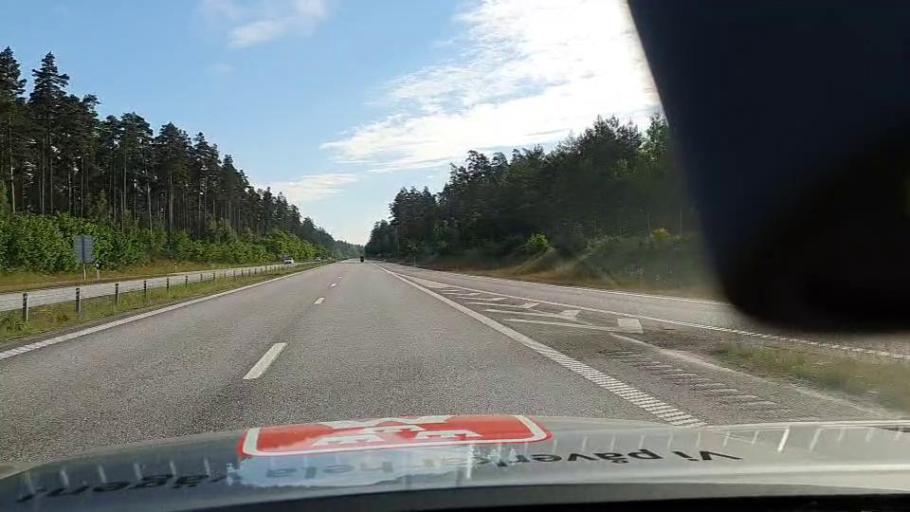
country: SE
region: Skane
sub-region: Bromolla Kommun
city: Bromoella
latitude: 56.0485
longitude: 14.4374
